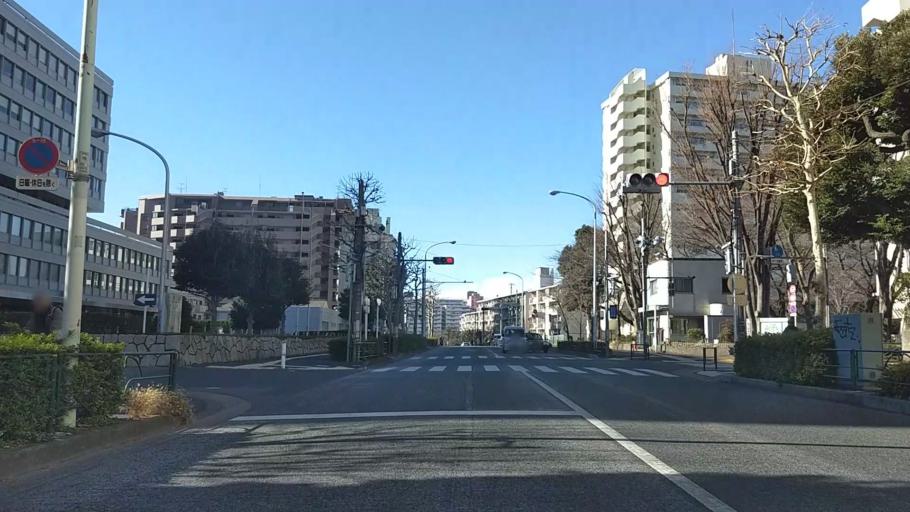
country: JP
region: Tokyo
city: Tokyo
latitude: 35.7013
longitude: 139.7154
